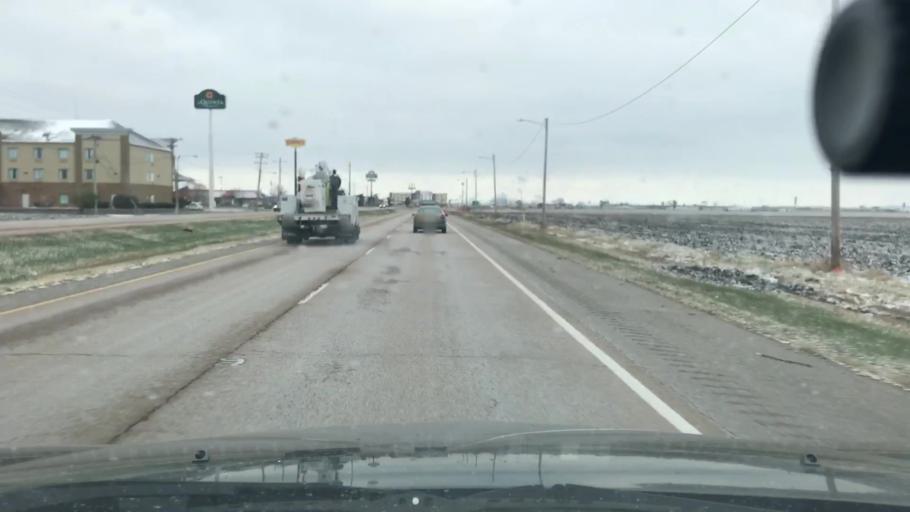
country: US
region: Illinois
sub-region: Madison County
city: Pontoon Beach
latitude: 38.7439
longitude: -90.0712
